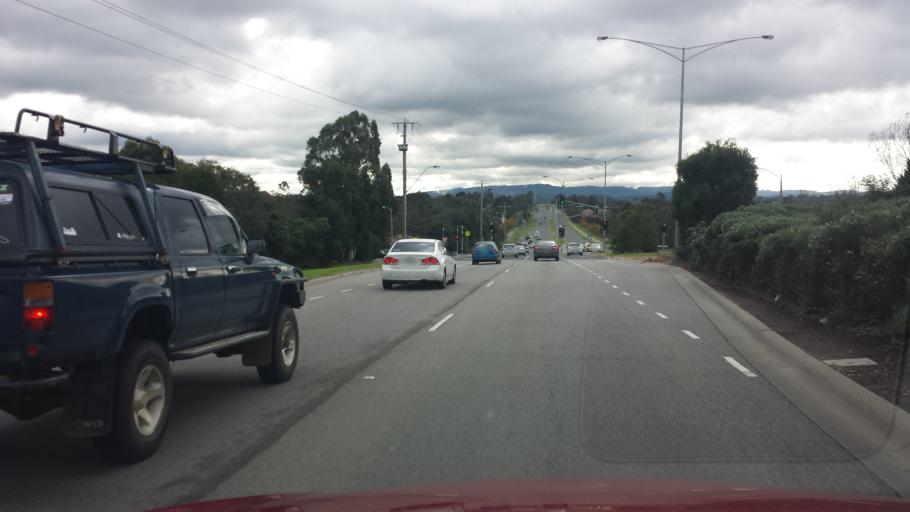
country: AU
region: Victoria
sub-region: Casey
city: Narre Warren
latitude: -38.0151
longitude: 145.3090
